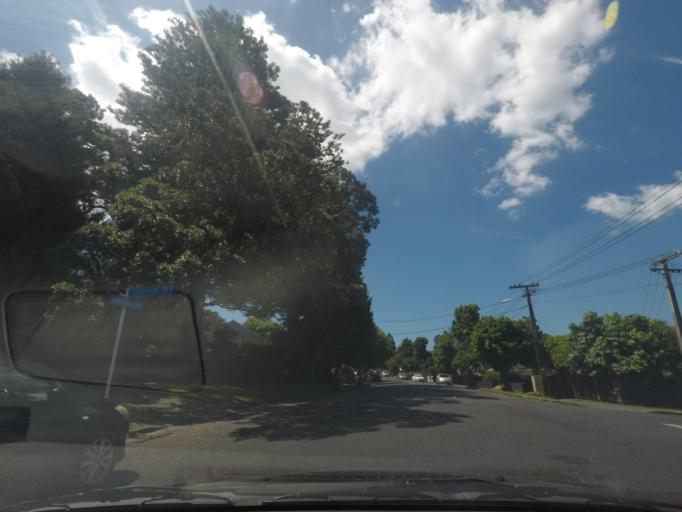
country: NZ
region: Auckland
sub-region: Auckland
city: Auckland
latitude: -36.9037
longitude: 174.7653
